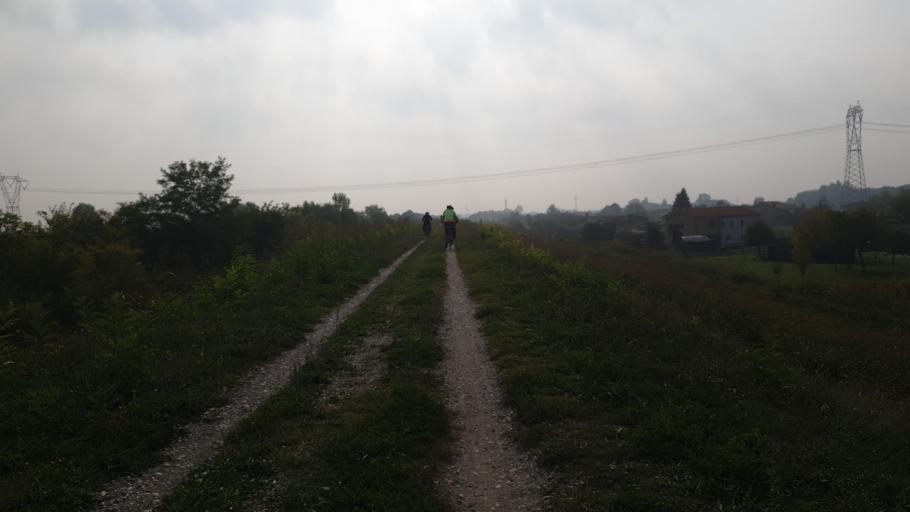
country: IT
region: Veneto
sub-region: Provincia di Venezia
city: Fosso
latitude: 45.3683
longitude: 12.0305
